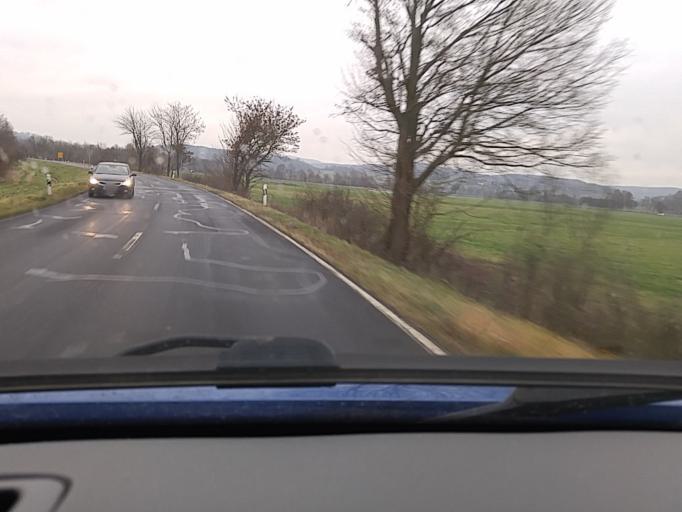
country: DE
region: Hesse
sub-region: Regierungsbezirk Darmstadt
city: Ranstadt
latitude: 50.3592
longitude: 8.9572
